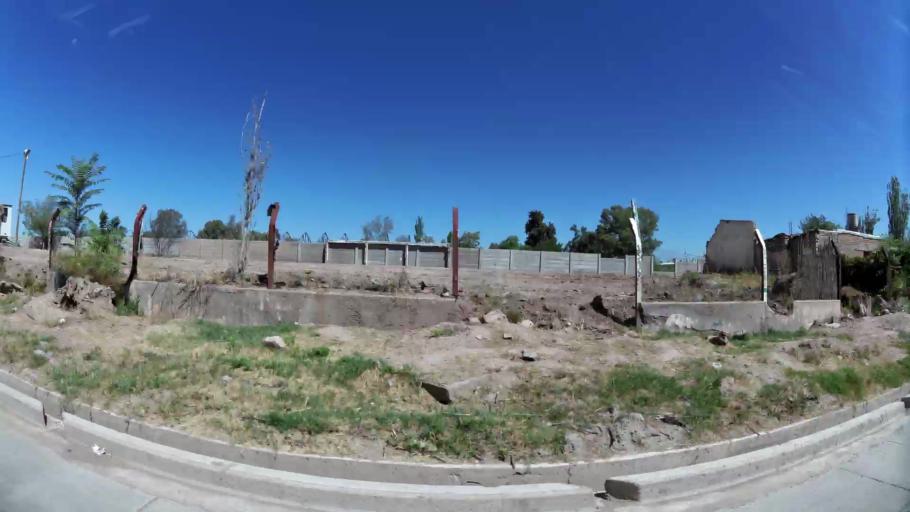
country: AR
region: Mendoza
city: Mendoza
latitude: -32.8852
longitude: -68.8114
